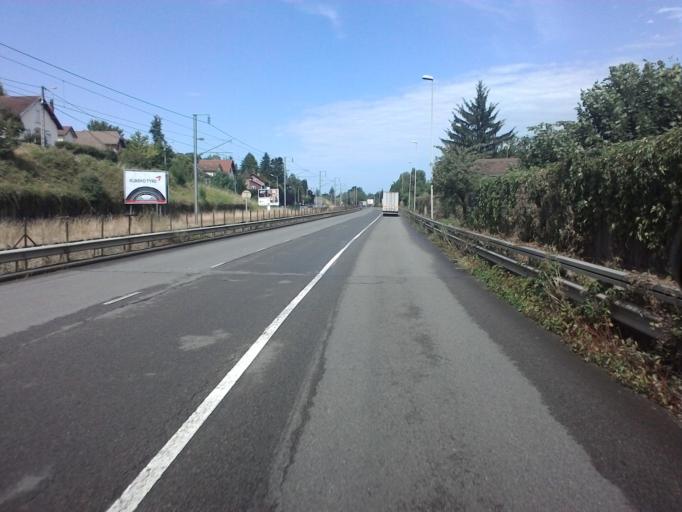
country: FR
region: Franche-Comte
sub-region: Departement du Jura
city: Lons-le-Saunier
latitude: 46.6687
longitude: 5.5628
